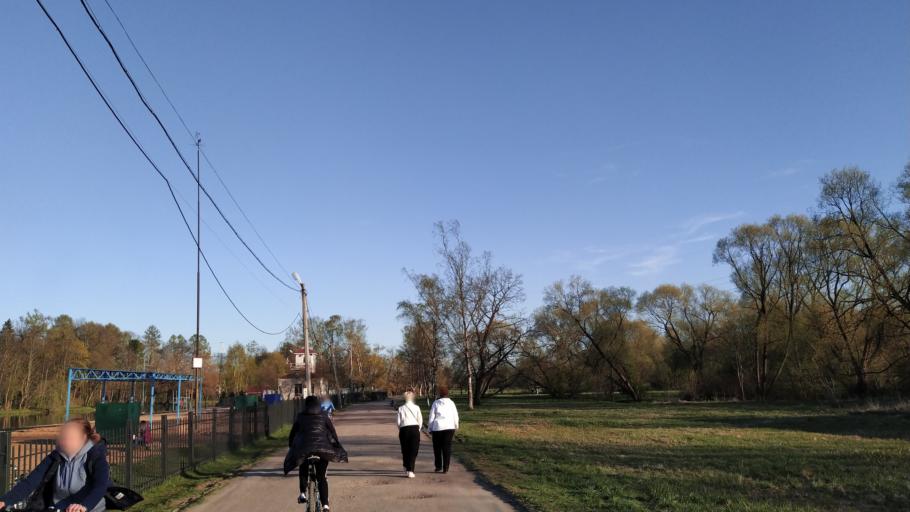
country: RU
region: St.-Petersburg
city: Pushkin
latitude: 59.7130
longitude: 30.4193
